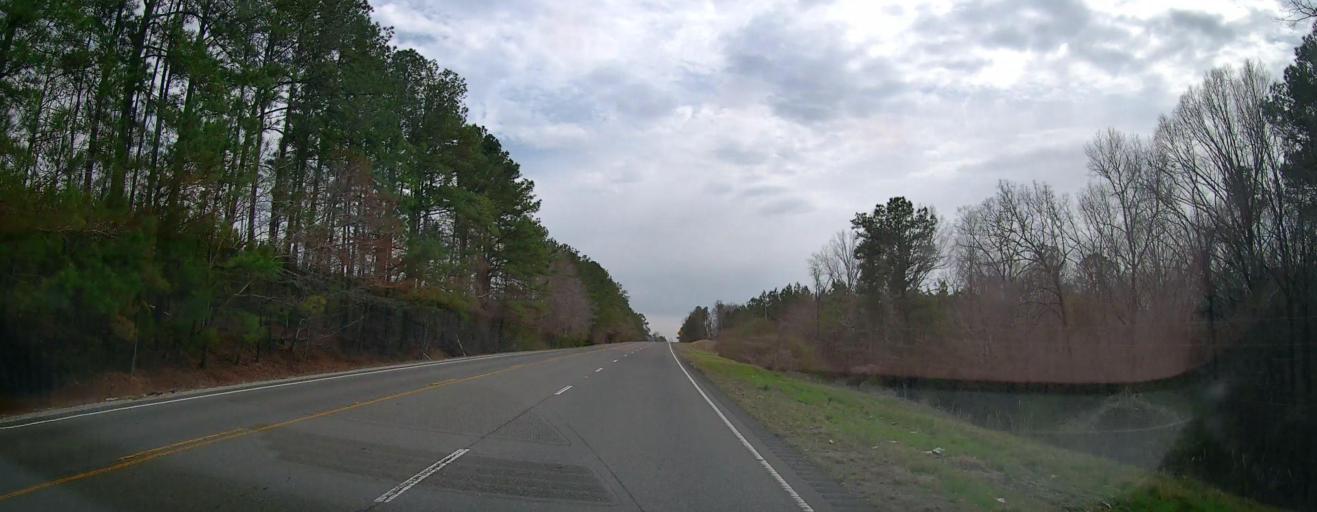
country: US
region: Alabama
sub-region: Marion County
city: Hamilton
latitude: 34.0588
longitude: -87.9676
